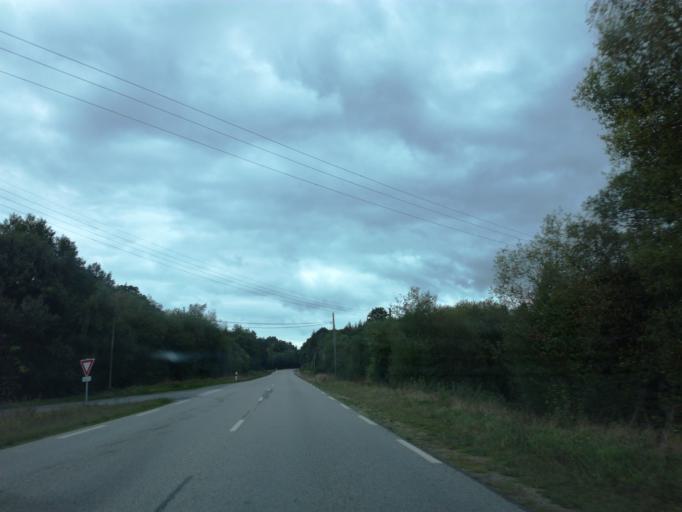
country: FR
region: Brittany
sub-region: Departement des Cotes-d'Armor
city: Plemet
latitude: 48.1707
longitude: -2.5866
